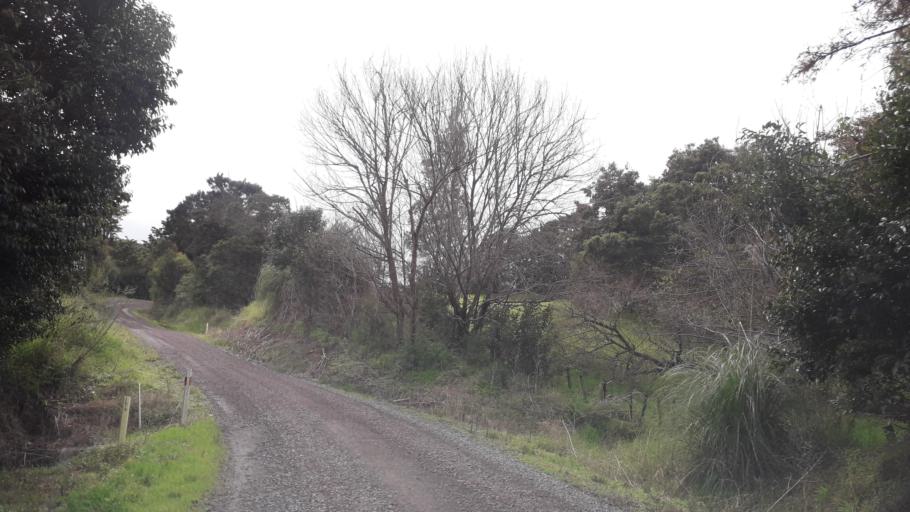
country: NZ
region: Northland
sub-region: Far North District
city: Waimate North
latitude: -35.3103
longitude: 173.5638
